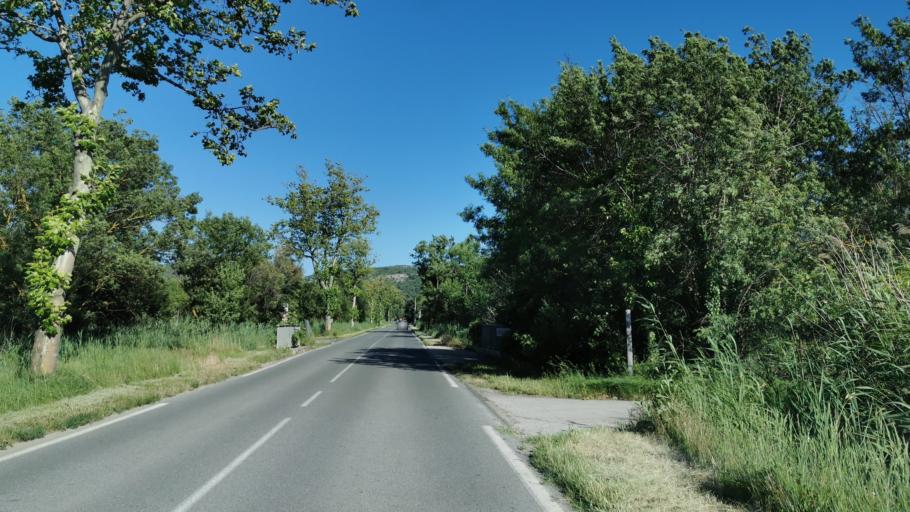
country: FR
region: Languedoc-Roussillon
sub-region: Departement de l'Aude
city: Vinassan
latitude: 43.1646
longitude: 3.0485
